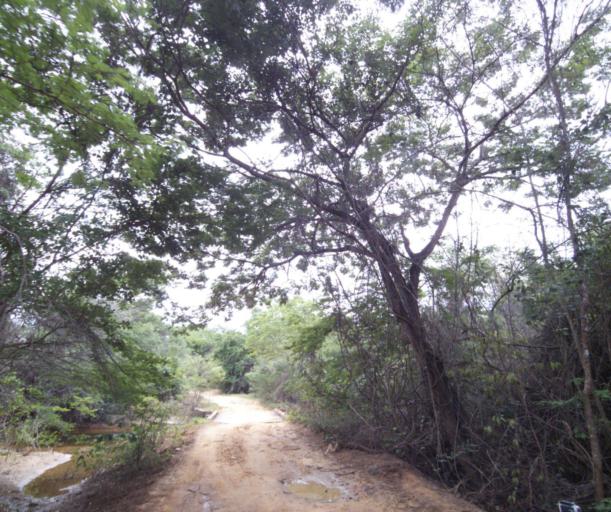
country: BR
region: Bahia
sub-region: Carinhanha
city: Carinhanha
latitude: -14.2509
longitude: -44.3701
